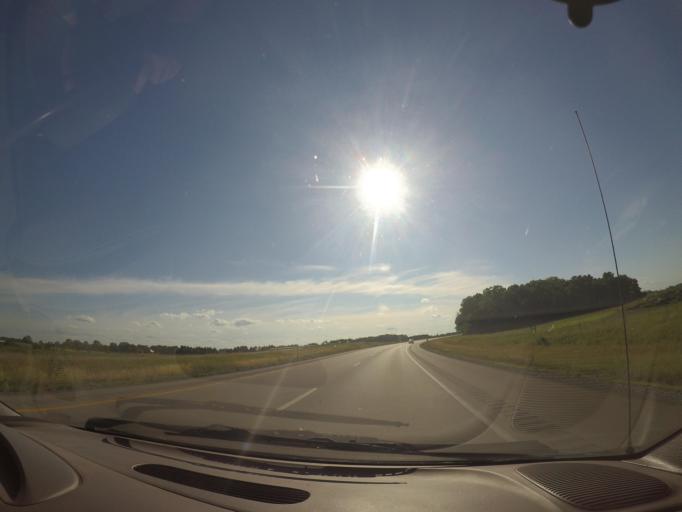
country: US
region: Ohio
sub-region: Henry County
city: Liberty Center
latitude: 41.4157
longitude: -84.0591
